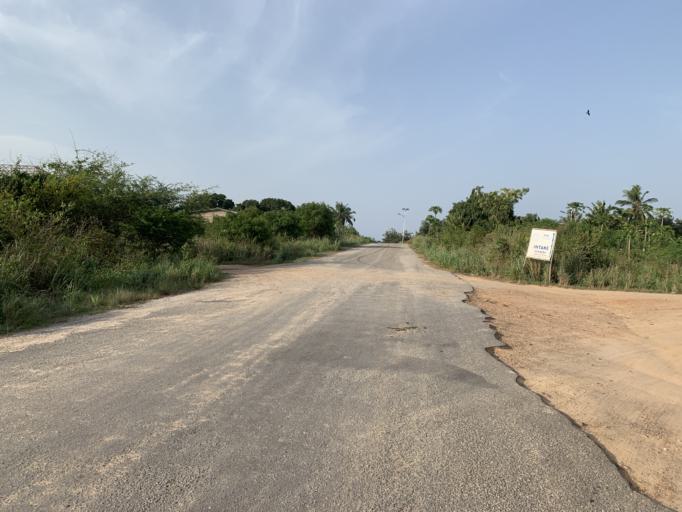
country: GH
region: Central
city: Winneba
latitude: 5.3901
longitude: -0.6023
